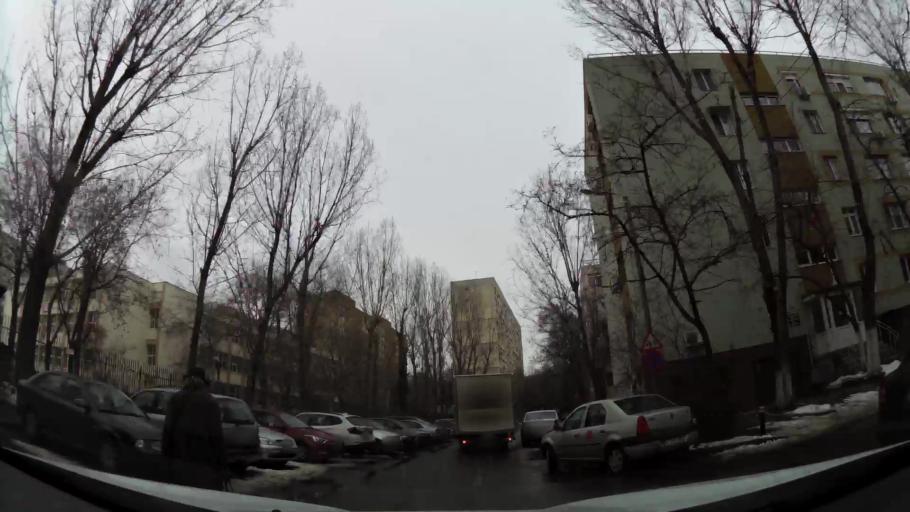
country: RO
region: Ilfov
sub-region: Comuna Chiajna
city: Rosu
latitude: 44.4211
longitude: 26.0256
